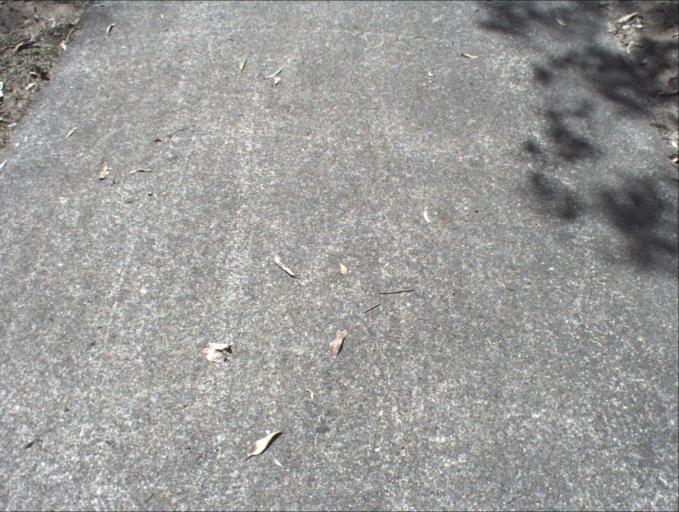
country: AU
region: Queensland
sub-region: Brisbane
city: Forest Lake
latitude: -27.6598
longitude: 153.0034
